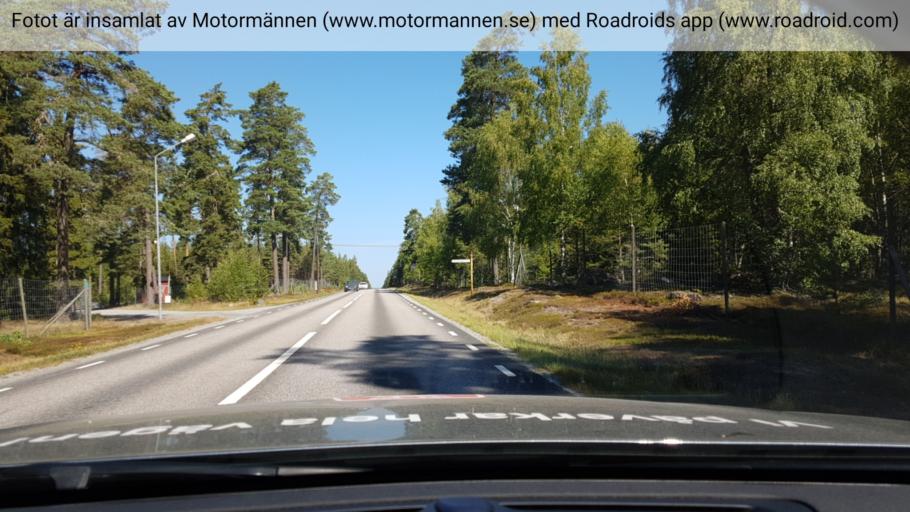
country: SE
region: Stockholm
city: Stenhamra
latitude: 59.3104
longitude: 17.6393
